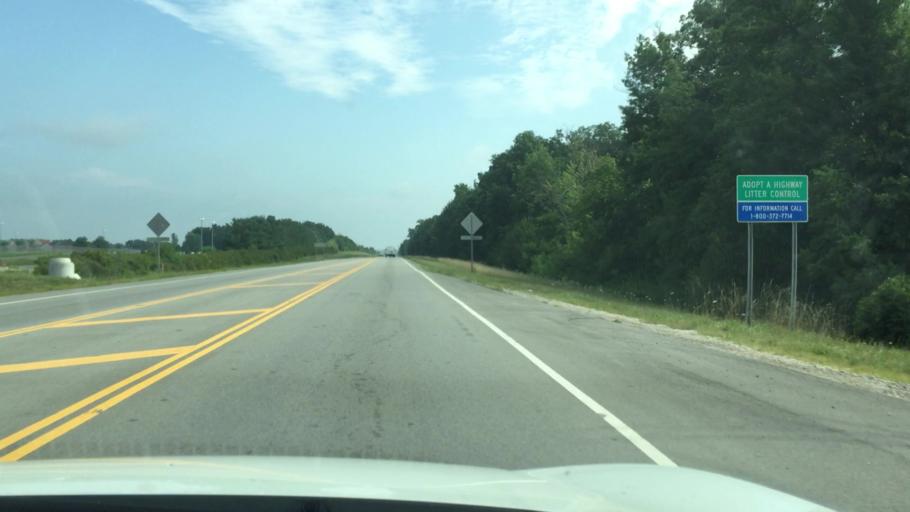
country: US
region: Ohio
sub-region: Union County
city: Marysville
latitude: 40.2276
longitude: -83.3979
